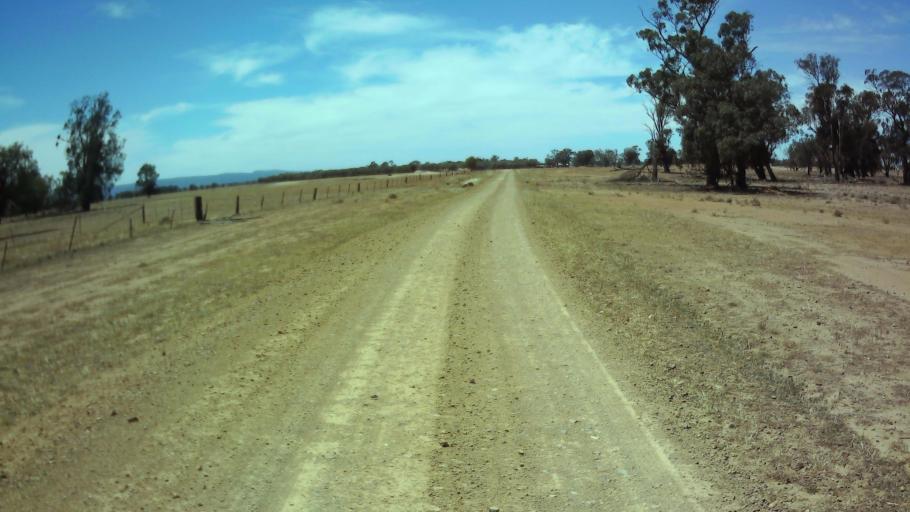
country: AU
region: New South Wales
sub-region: Weddin
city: Grenfell
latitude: -33.8631
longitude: 147.7594
